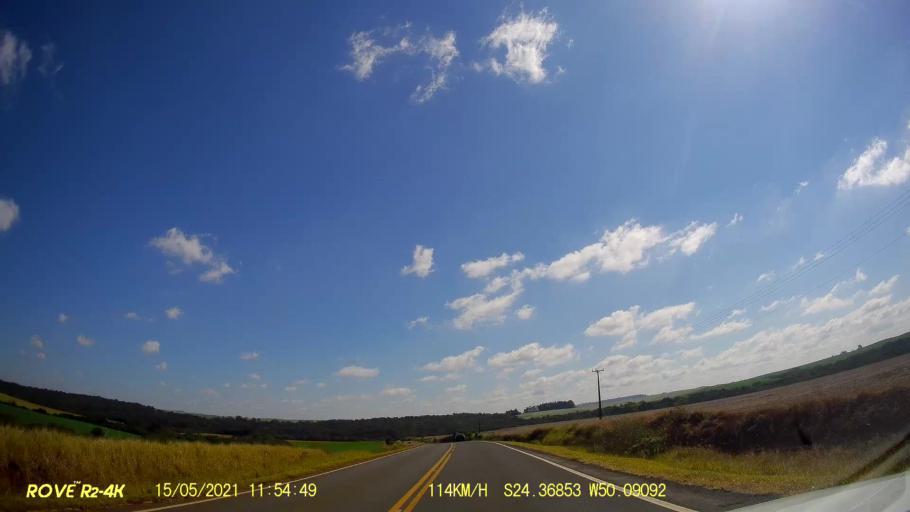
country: BR
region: Parana
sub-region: Pirai Do Sul
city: Pirai do Sul
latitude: -24.3686
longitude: -50.0907
